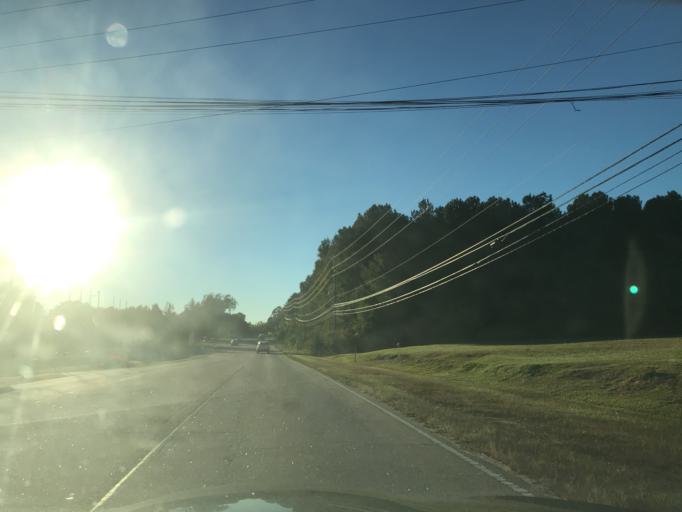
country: US
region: North Carolina
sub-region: Wake County
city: Garner
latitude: 35.7474
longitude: -78.5967
